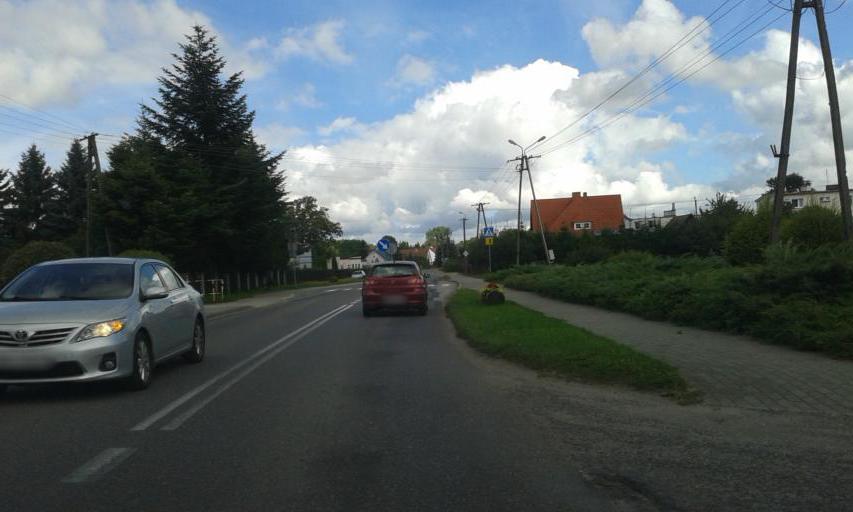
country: PL
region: West Pomeranian Voivodeship
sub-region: Powiat slawienski
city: Slawno
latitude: 54.2744
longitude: 16.6714
